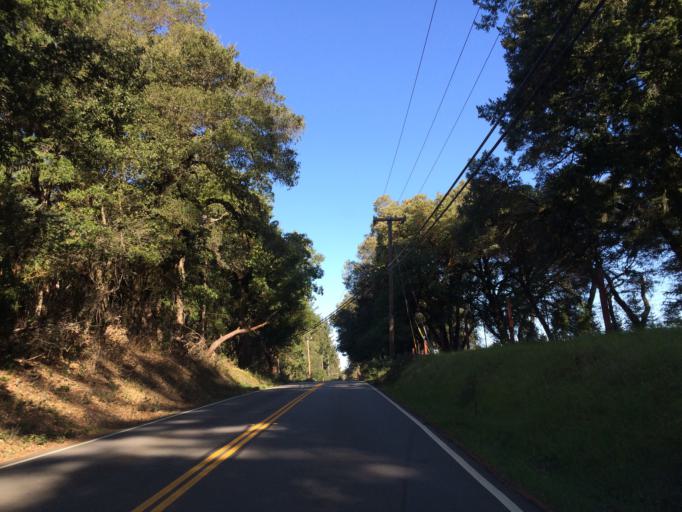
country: US
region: California
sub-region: Santa Cruz County
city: Boulder Creek
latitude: 37.1151
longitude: -122.1545
